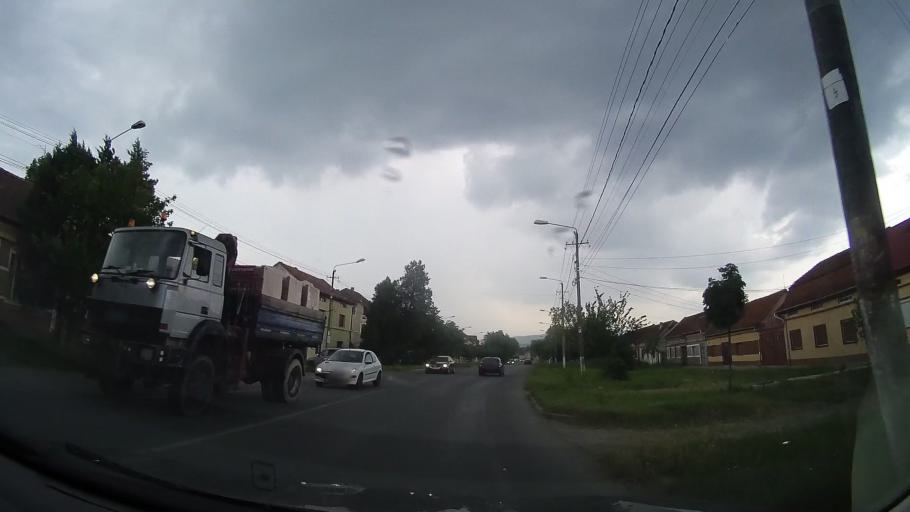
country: RO
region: Caras-Severin
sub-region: Municipiul Caransebes
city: Caransebes
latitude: 45.4049
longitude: 22.2242
